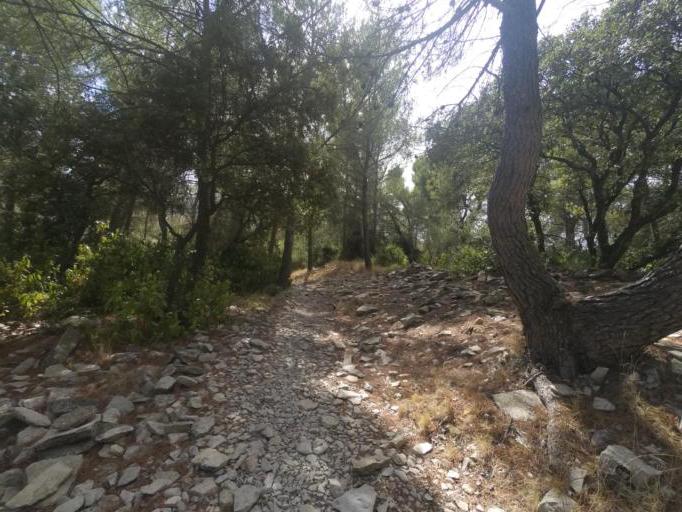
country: FR
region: Languedoc-Roussillon
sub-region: Departement du Gard
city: Nages-et-Solorgues
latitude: 43.7937
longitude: 4.2273
